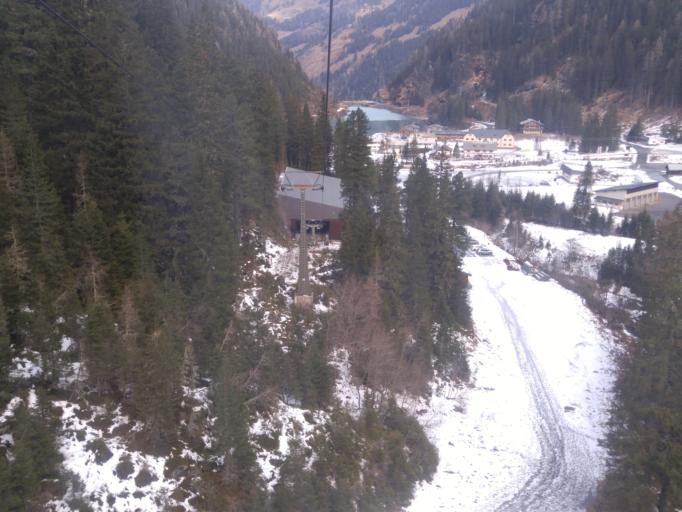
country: AT
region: Salzburg
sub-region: Politischer Bezirk Zell am See
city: Niedernsill
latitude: 47.1681
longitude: 12.6243
